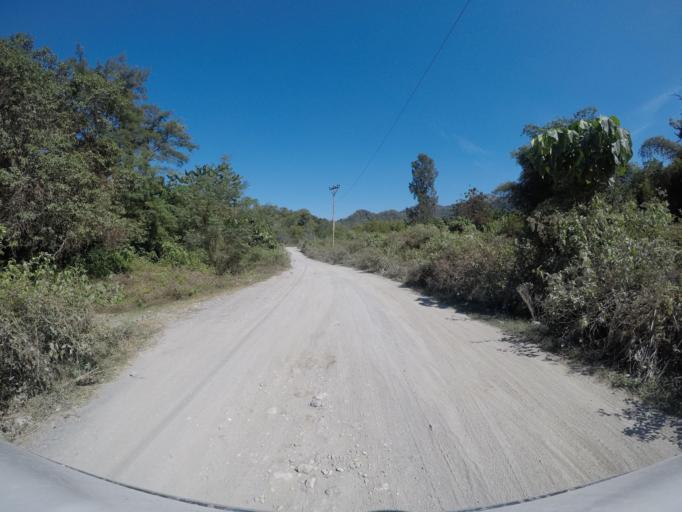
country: TL
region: Manufahi
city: Same
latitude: -8.9586
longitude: 126.0085
